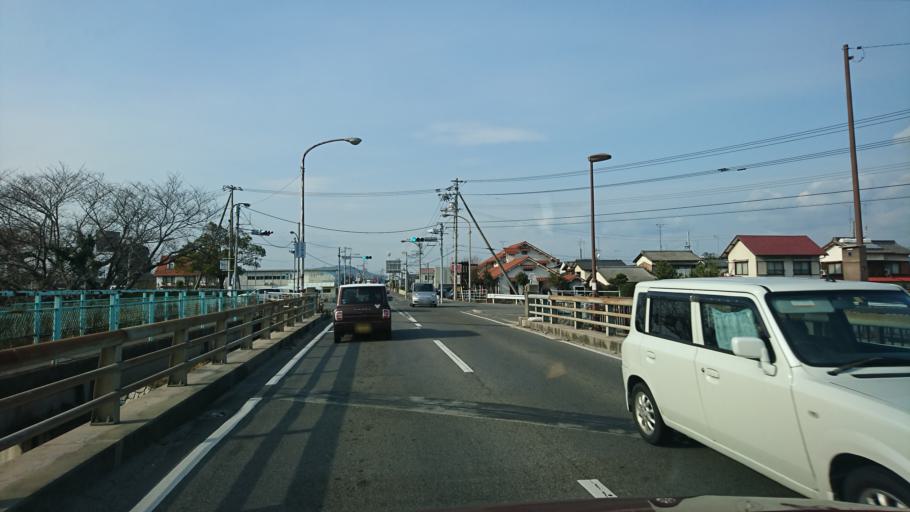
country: JP
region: Ehime
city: Saijo
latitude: 34.0380
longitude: 133.0315
